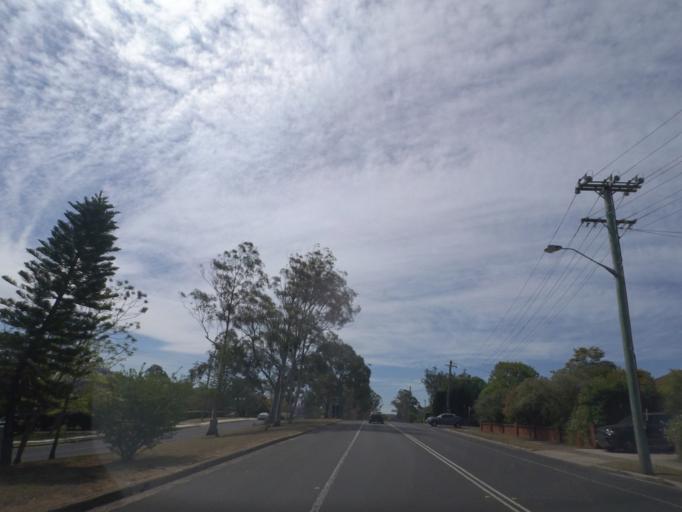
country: AU
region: New South Wales
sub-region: Camden
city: Camden South
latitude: -34.0664
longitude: 150.6938
